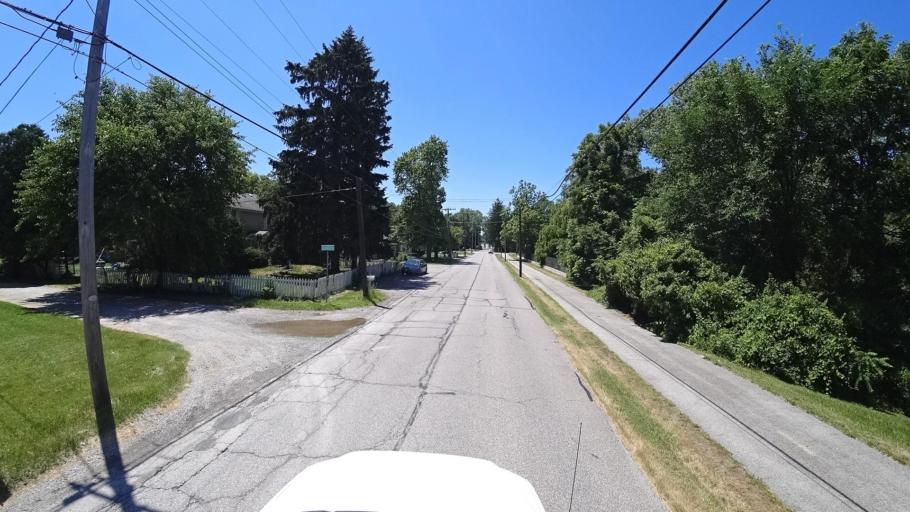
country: US
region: Indiana
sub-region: Porter County
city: Chesterton
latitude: 41.6167
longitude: -87.0654
